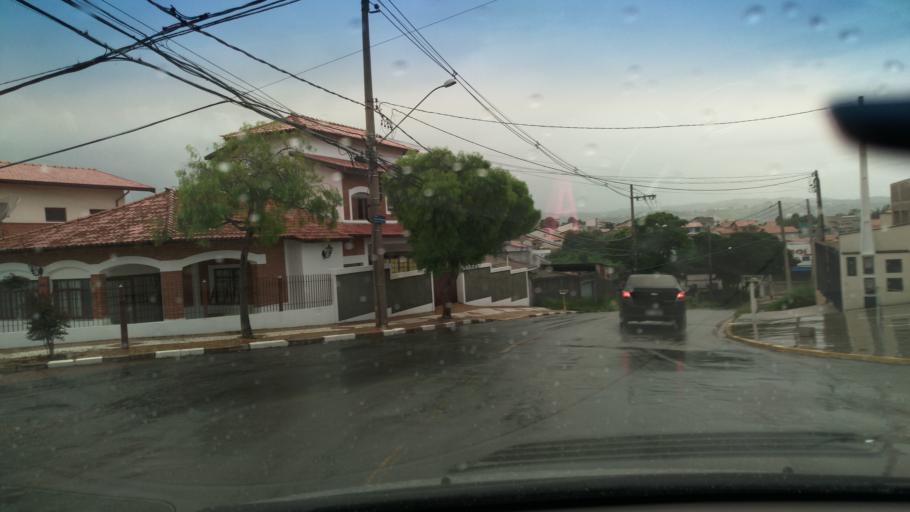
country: BR
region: Sao Paulo
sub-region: Valinhos
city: Valinhos
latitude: -22.9555
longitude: -46.9992
